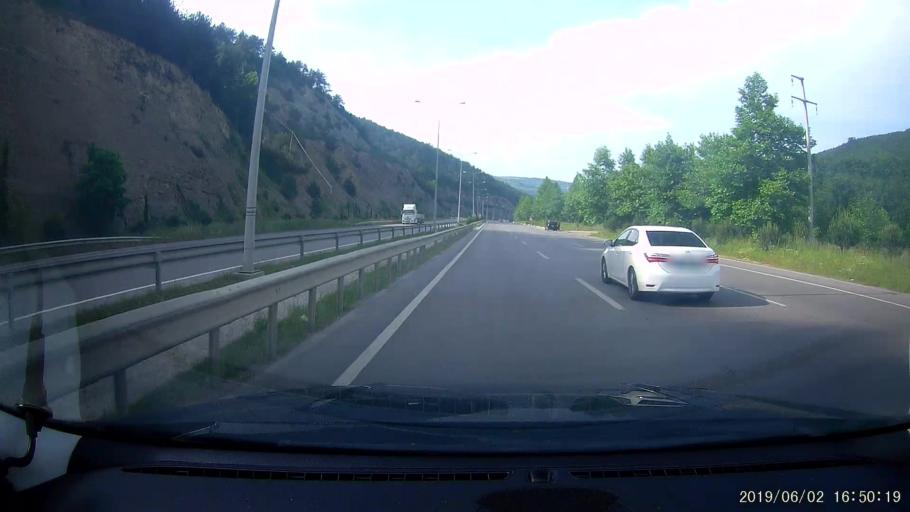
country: TR
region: Samsun
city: Samsun
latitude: 41.2522
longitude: 36.1736
